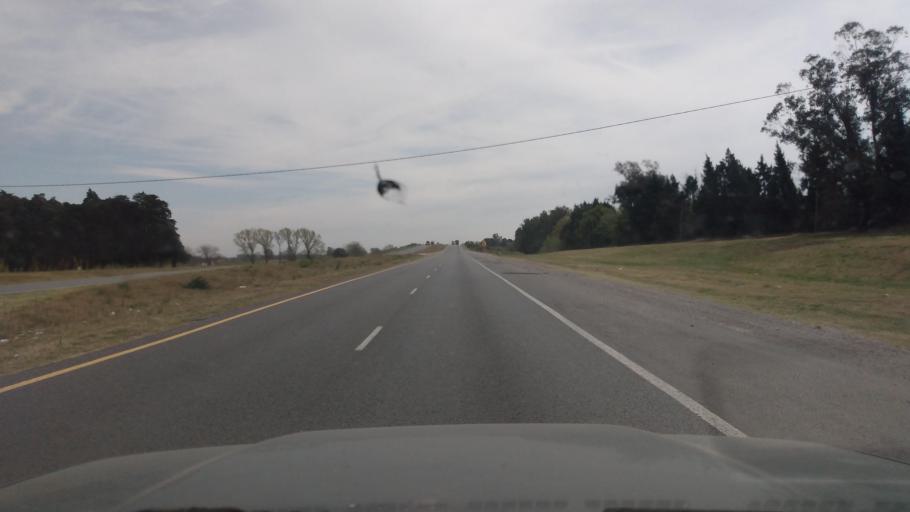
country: AR
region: Buenos Aires
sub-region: Partido de Lujan
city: Lujan
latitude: -34.4855
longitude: -59.0575
